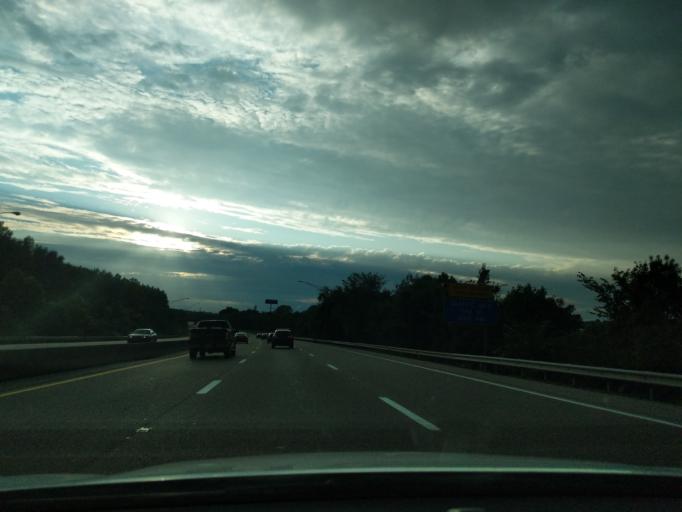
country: US
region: Tennessee
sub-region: Shelby County
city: New South Memphis
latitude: 35.0774
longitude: -90.0469
